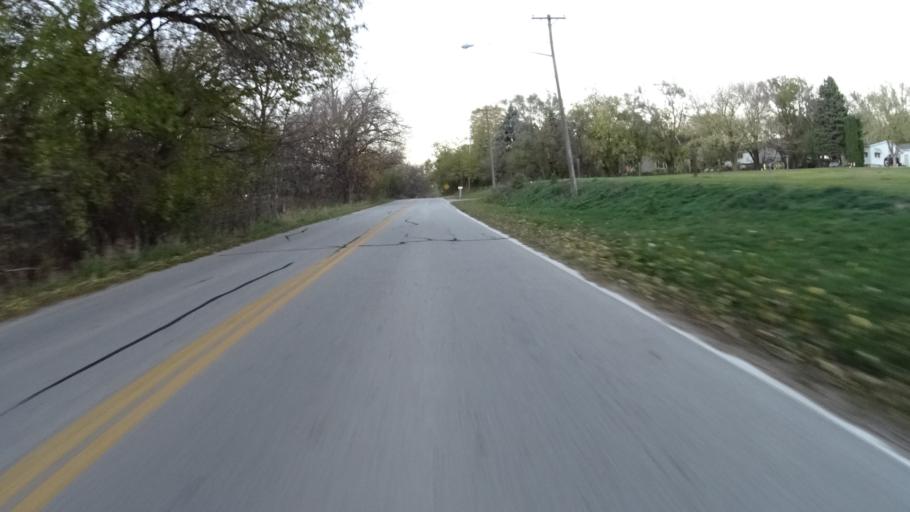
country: US
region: Nebraska
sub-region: Sarpy County
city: Offutt Air Force Base
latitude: 41.1810
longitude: -95.9527
